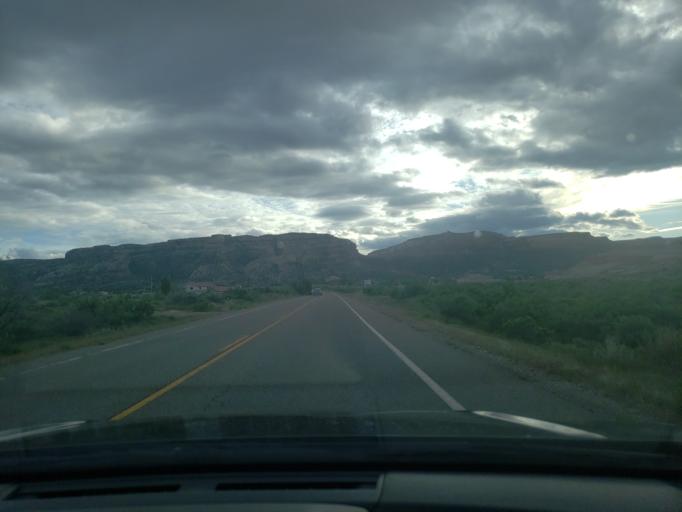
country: US
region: Colorado
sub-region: Mesa County
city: Redlands
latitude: 39.0463
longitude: -108.6197
